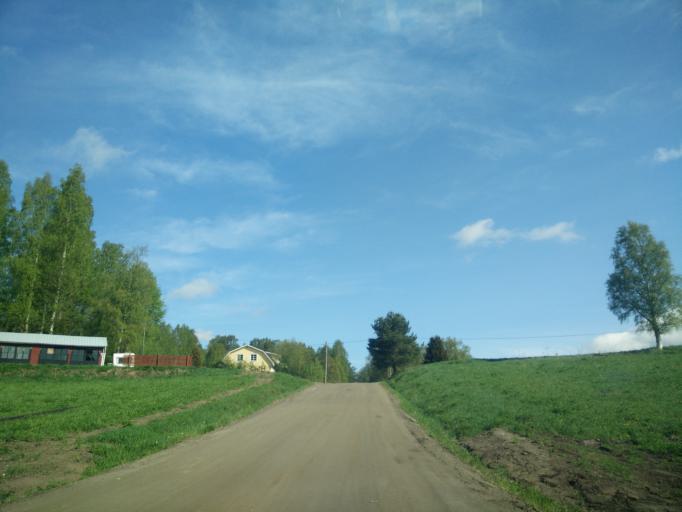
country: SE
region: Vaesternorrland
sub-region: Sundsvalls Kommun
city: Vi
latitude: 62.3103
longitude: 17.2331
